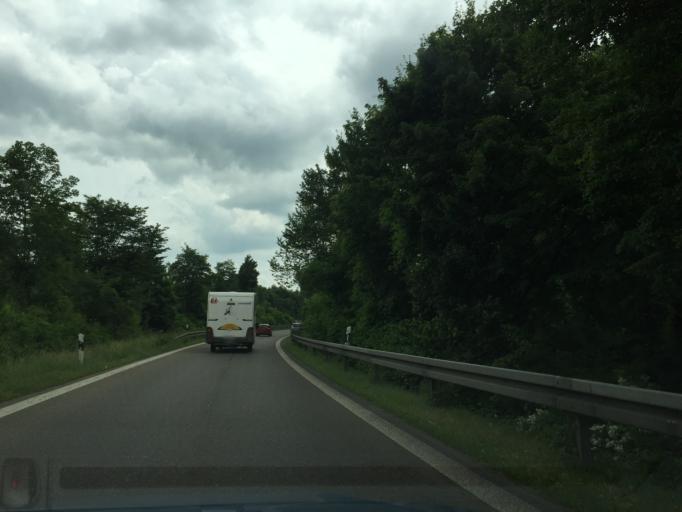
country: DE
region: Bavaria
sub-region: Swabia
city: Neu-Ulm
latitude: 48.3689
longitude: 9.9953
